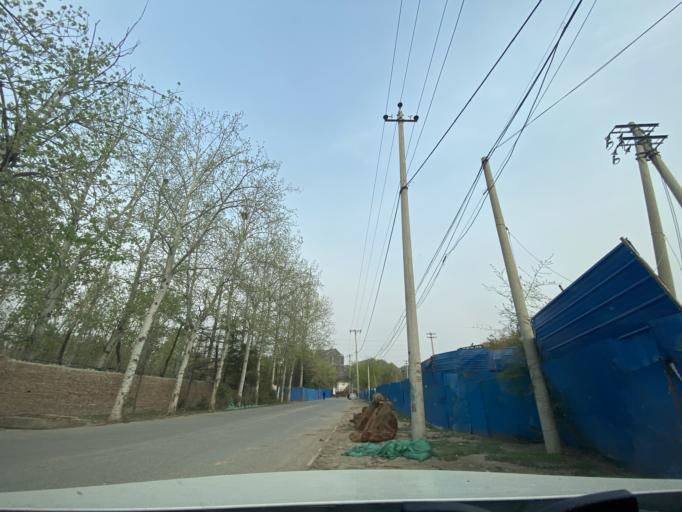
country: CN
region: Beijing
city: Babaoshan
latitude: 39.9328
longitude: 116.2303
